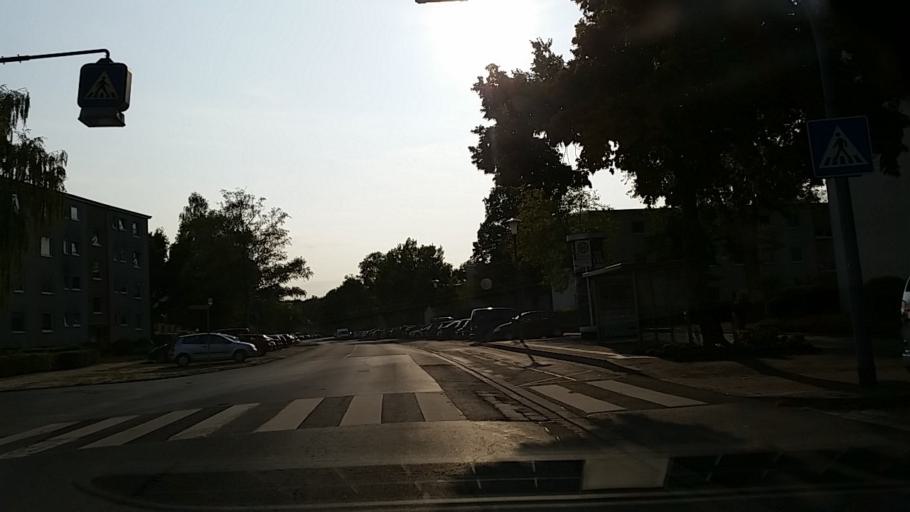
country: DE
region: Lower Saxony
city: Wolfsburg
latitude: 52.4061
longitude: 10.7818
